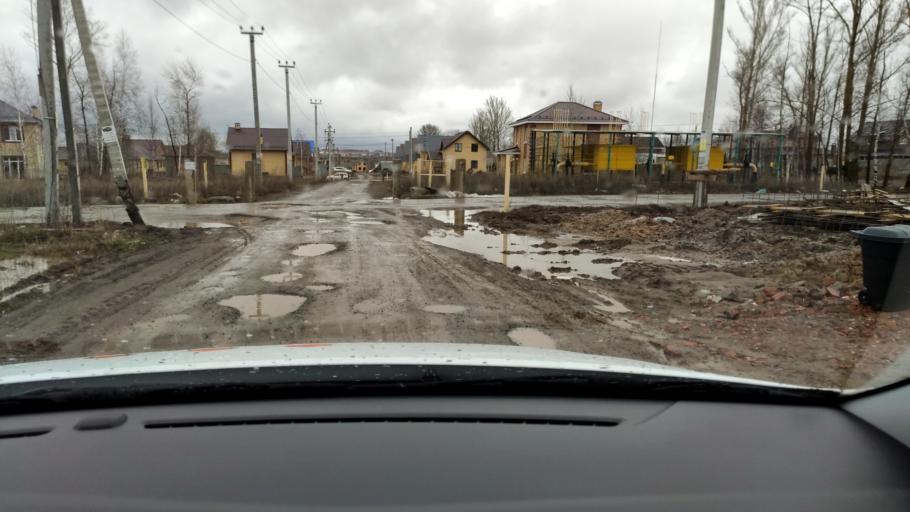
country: RU
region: Tatarstan
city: Stolbishchi
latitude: 55.7185
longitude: 49.3050
